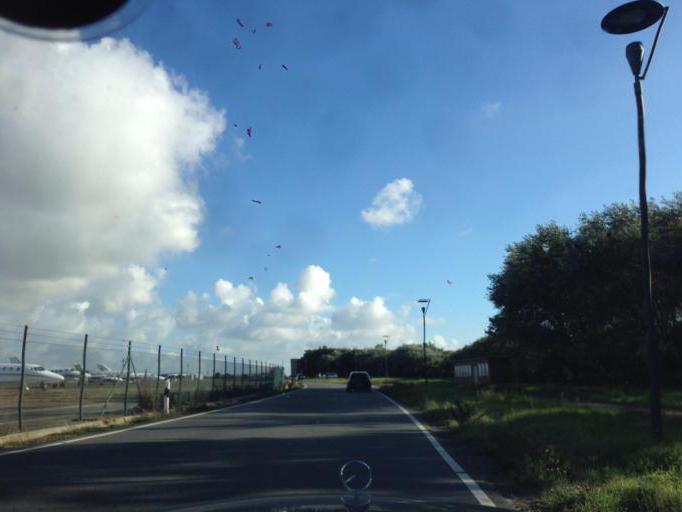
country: DE
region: Schleswig-Holstein
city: Tinnum
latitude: 54.9141
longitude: 8.3238
